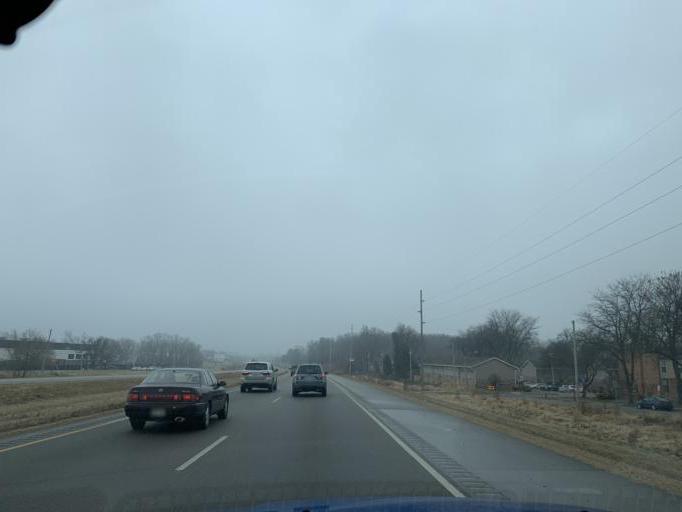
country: US
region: Wisconsin
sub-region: Dane County
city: Monona
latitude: 43.0596
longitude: -89.3096
